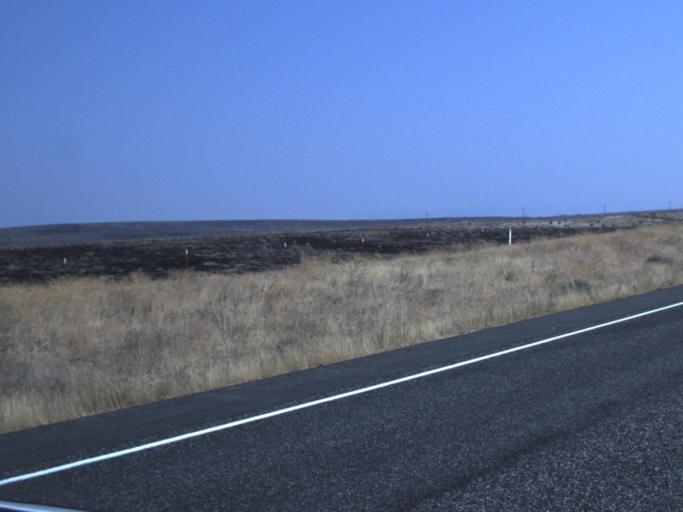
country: US
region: Washington
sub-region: Grant County
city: Desert Aire
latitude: 46.5730
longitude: -119.7632
